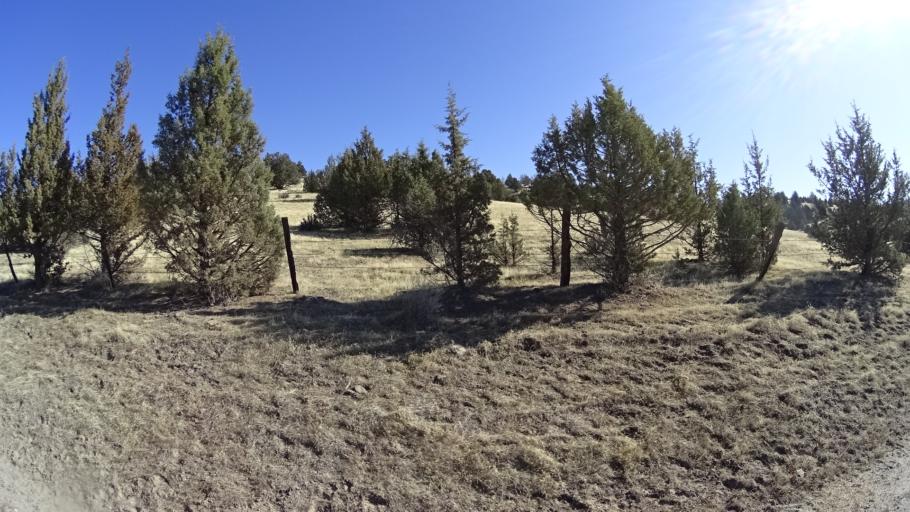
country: US
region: California
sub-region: Siskiyou County
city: Montague
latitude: 41.7183
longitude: -122.3722
